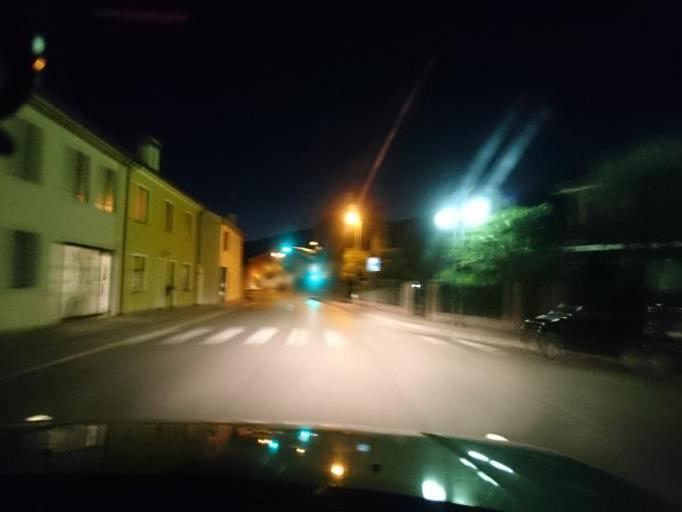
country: IT
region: Veneto
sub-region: Provincia di Padova
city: Baone
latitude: 45.2436
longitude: 11.6873
